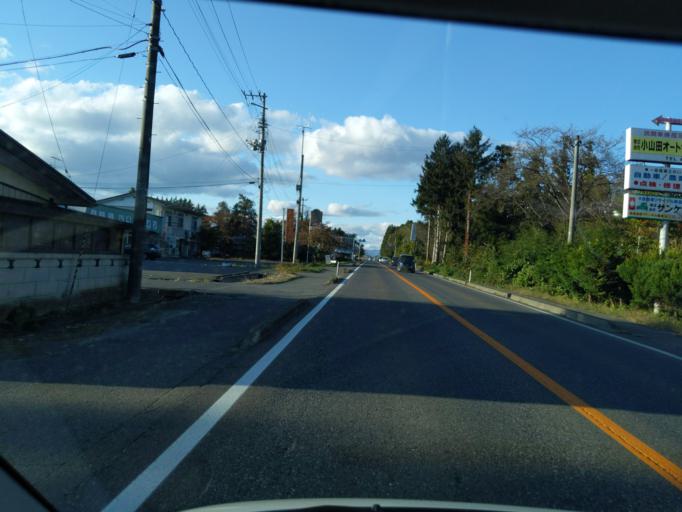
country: JP
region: Iwate
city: Kitakami
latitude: 39.2094
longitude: 141.1065
